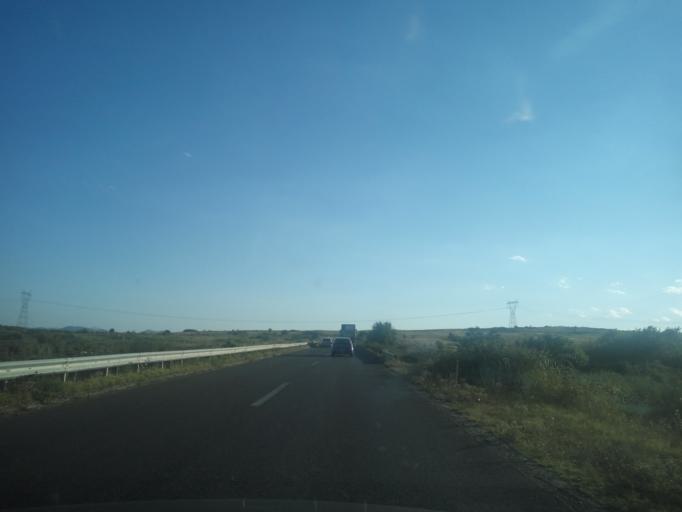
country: XK
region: Gjakova
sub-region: Komuna e Gjakoves
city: Gjakove
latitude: 42.4509
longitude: 20.4981
